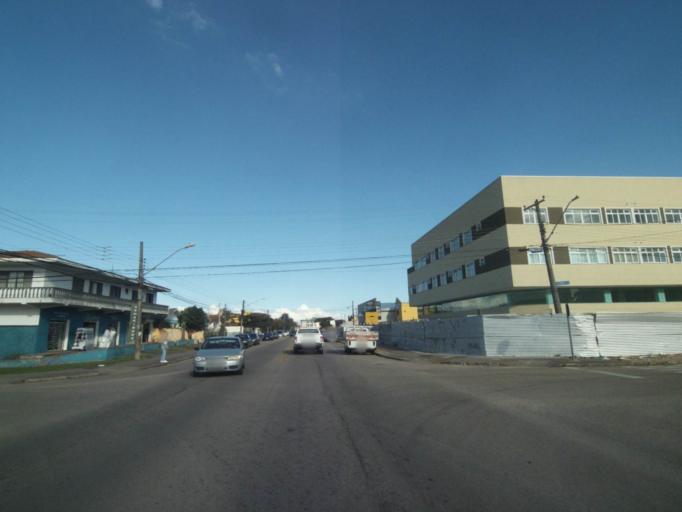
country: BR
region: Parana
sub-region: Pinhais
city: Pinhais
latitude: -25.4426
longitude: -49.2102
